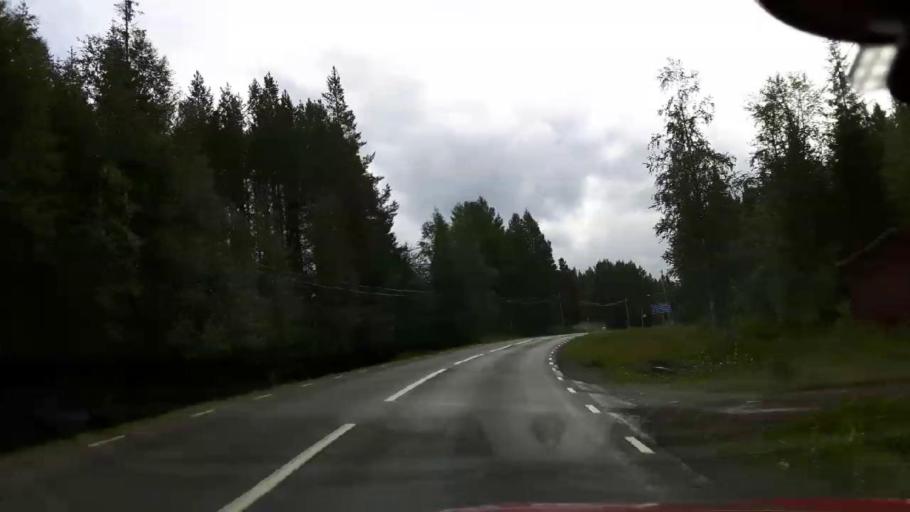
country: NO
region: Nord-Trondelag
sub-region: Lierne
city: Sandvika
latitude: 64.5085
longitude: 14.1577
